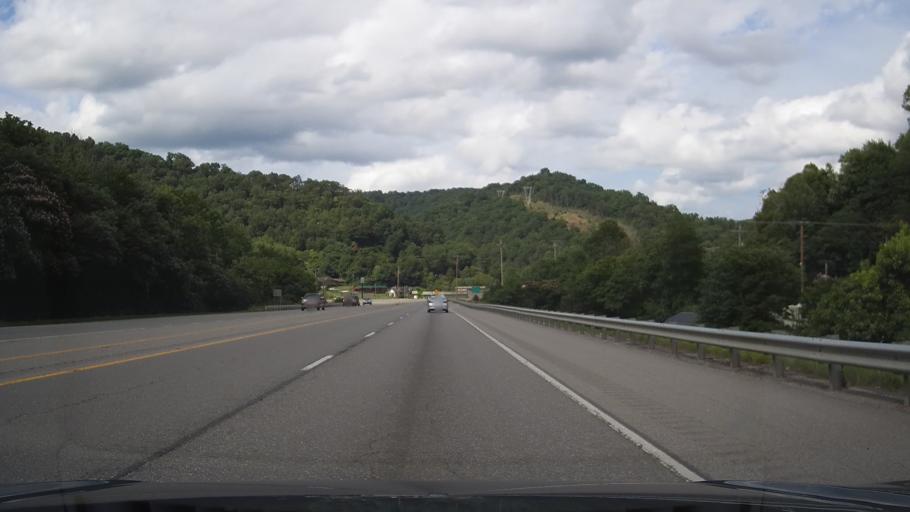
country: US
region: Kentucky
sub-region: Pike County
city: Coal Run Village
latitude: 37.5678
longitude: -82.6427
